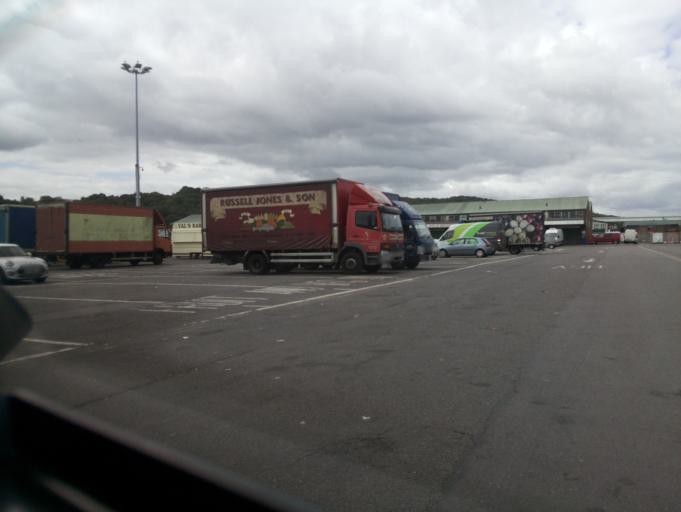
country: GB
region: Wales
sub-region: Cardiff
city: Cardiff
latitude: 51.4666
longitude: -3.1972
